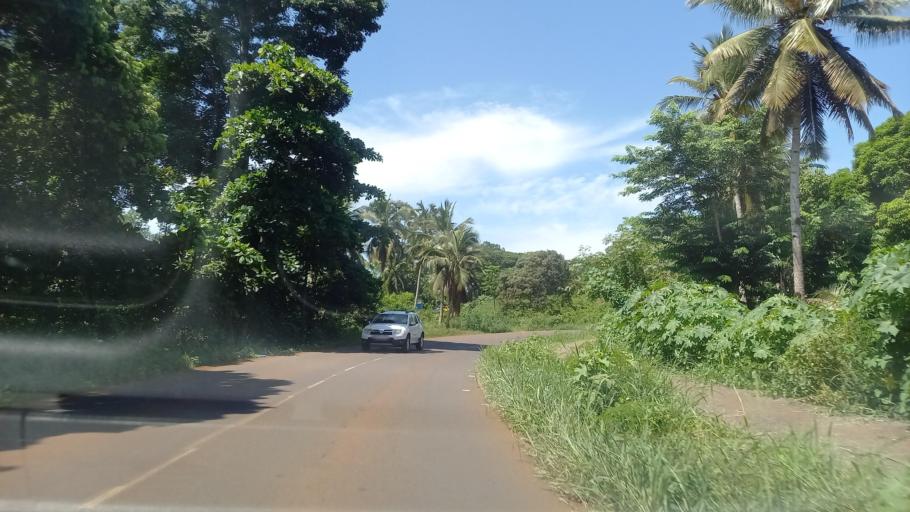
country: YT
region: Tsingoni
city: Tsingoni
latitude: -12.7933
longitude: 45.1230
